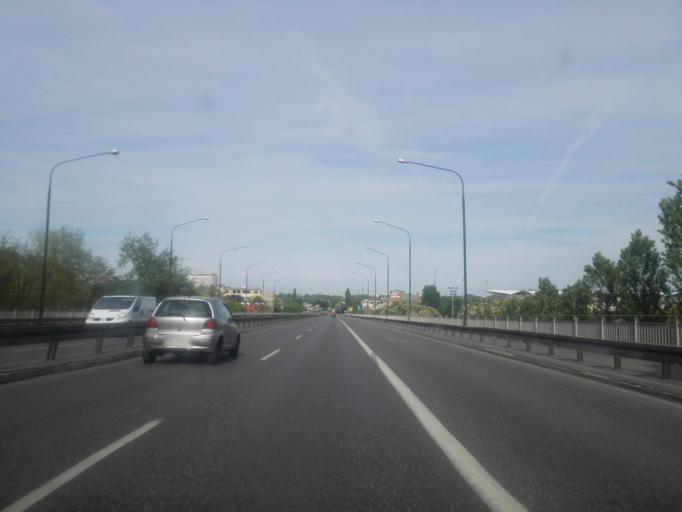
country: PL
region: Masovian Voivodeship
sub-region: Warszawa
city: Srodmiescie
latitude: 52.2207
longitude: 21.0313
